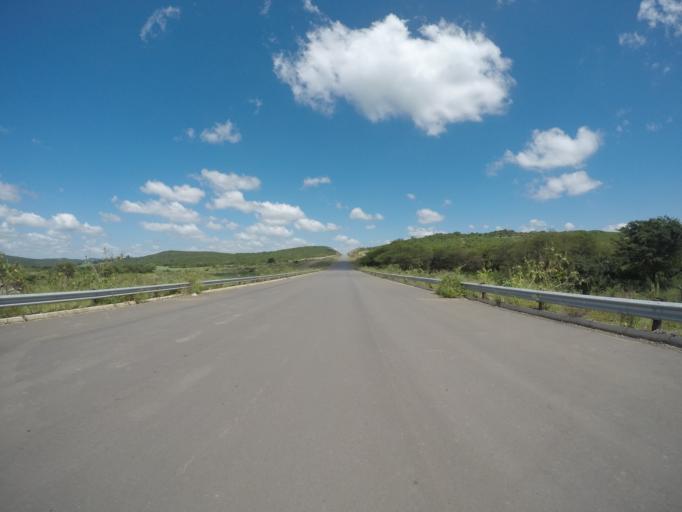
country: ZA
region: KwaZulu-Natal
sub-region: uThungulu District Municipality
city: Empangeni
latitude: -28.6183
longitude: 31.7557
